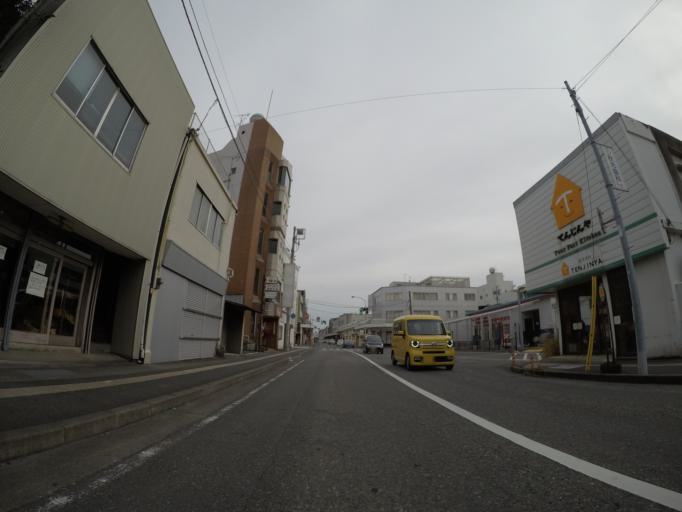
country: JP
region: Shizuoka
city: Fuji
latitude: 35.1638
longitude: 138.6834
